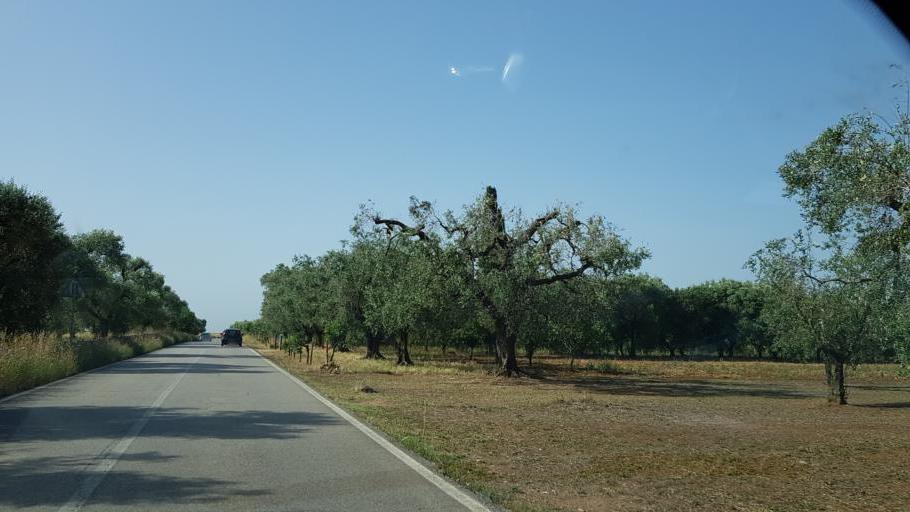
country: IT
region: Apulia
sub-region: Provincia di Brindisi
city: Mesagne
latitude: 40.5133
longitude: 17.8265
